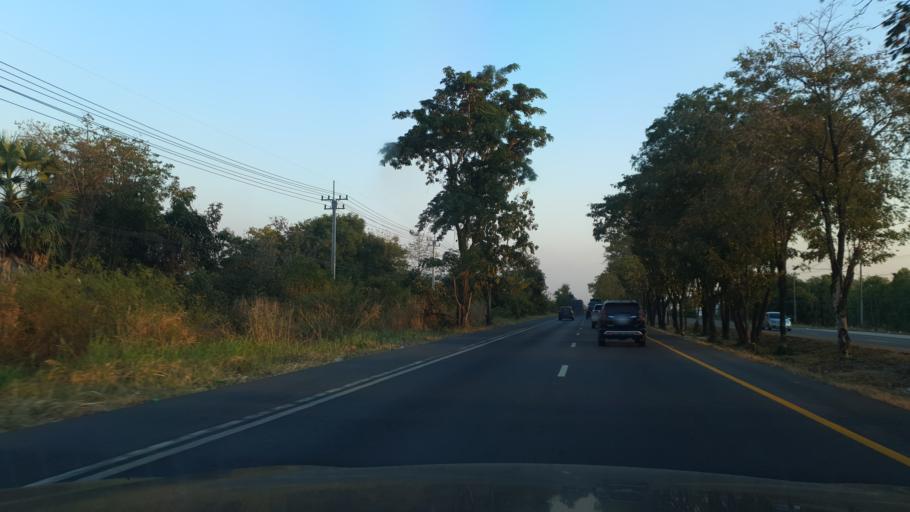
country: TH
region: Nakhon Sawan
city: Banphot Phisai
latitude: 15.8283
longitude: 99.9361
